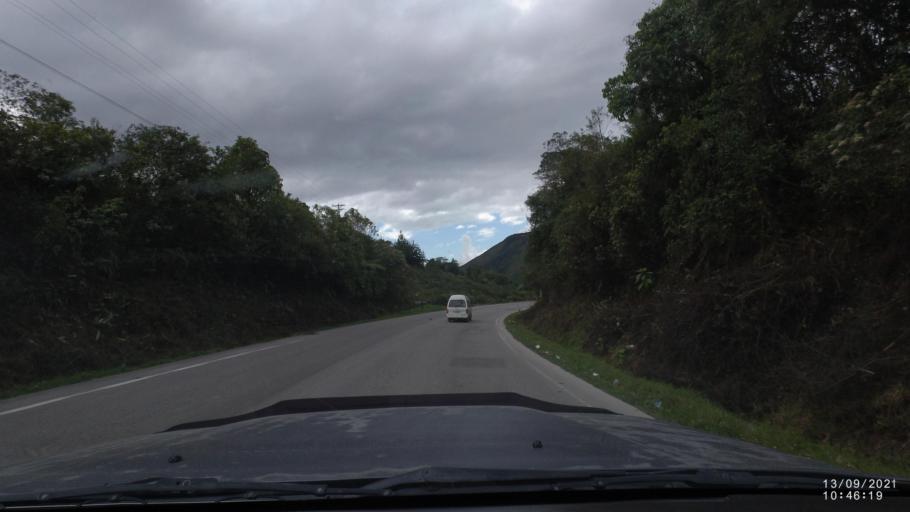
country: BO
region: Cochabamba
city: Colomi
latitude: -17.2031
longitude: -65.8670
